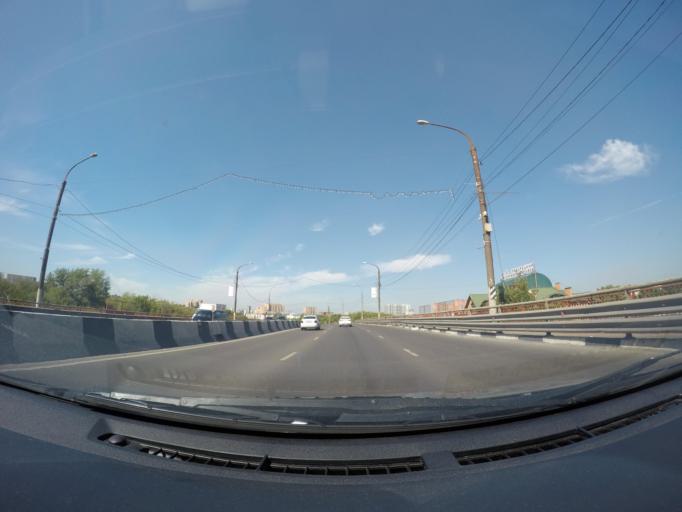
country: RU
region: Moskovskaya
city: Lyubertsy
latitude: 55.6740
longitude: 37.9039
